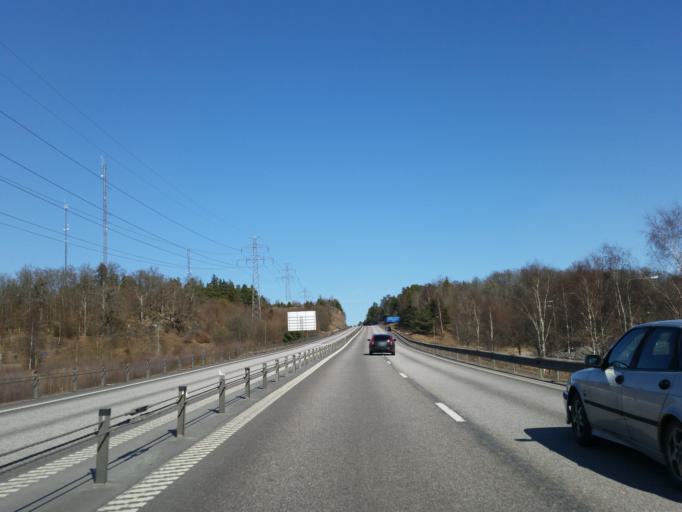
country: SE
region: Kalmar
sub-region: Oskarshamns Kommun
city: Oskarshamn
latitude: 57.2671
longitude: 16.4316
